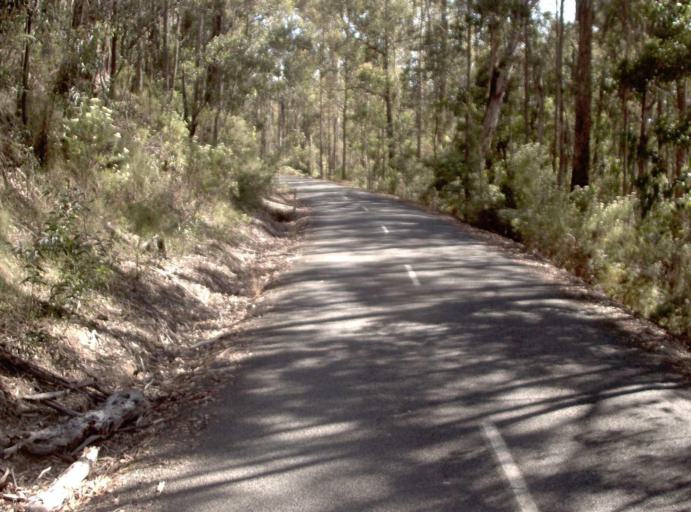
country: AU
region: New South Wales
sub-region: Bombala
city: Bombala
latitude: -37.3862
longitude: 148.6256
